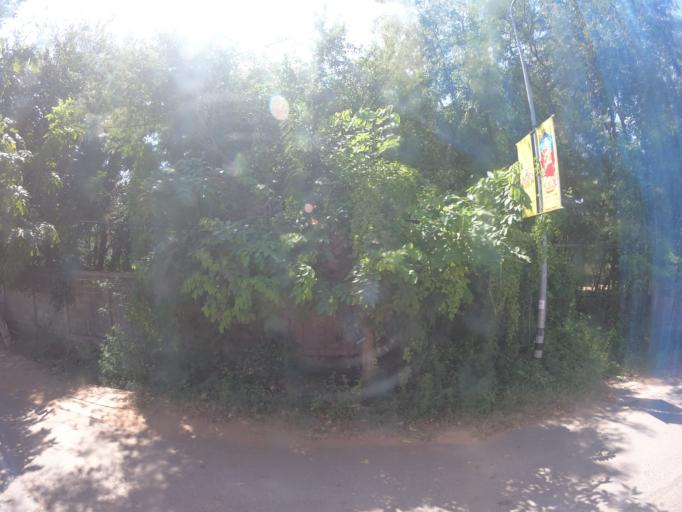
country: TH
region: Khon Kaen
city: Ban Phai
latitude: 16.0675
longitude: 102.7213
